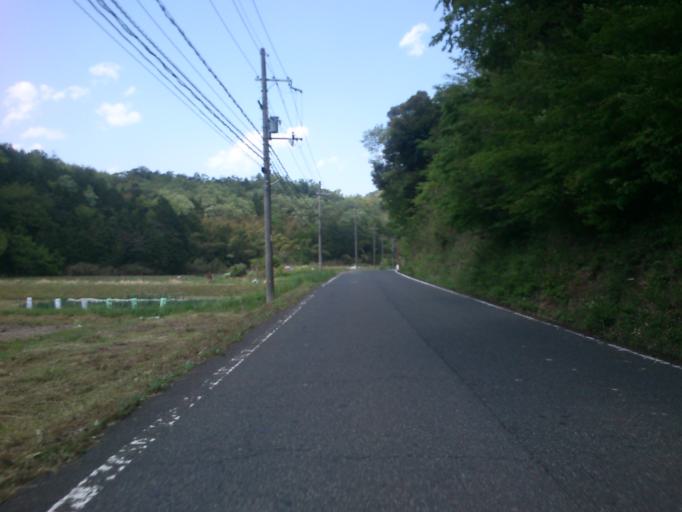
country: JP
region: Kyoto
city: Miyazu
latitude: 35.6827
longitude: 135.1109
